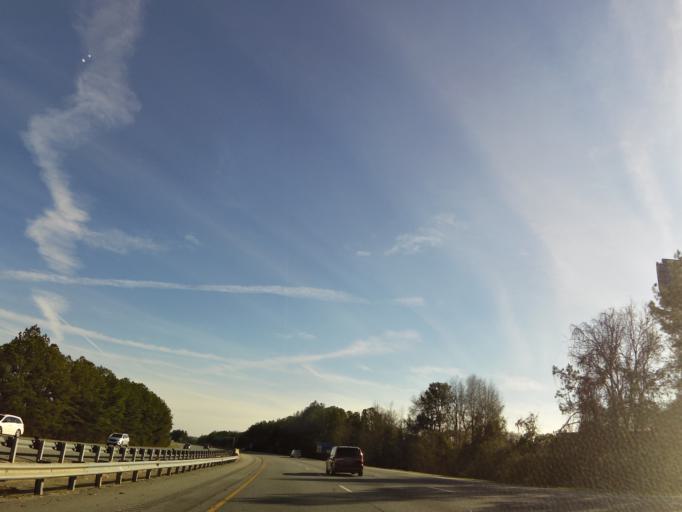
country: US
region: Alabama
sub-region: Russell County
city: Phenix City
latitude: 32.5265
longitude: -84.9592
